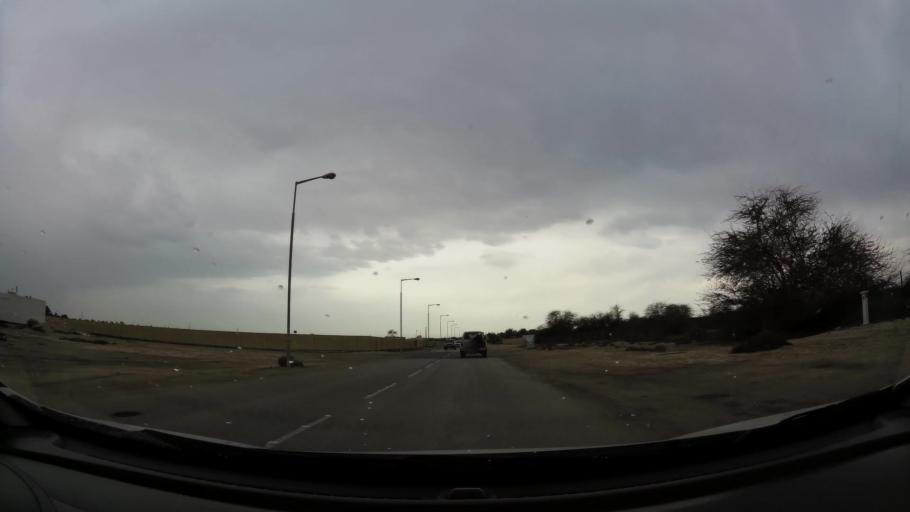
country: BH
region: Central Governorate
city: Madinat Hamad
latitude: 26.1645
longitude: 50.4576
